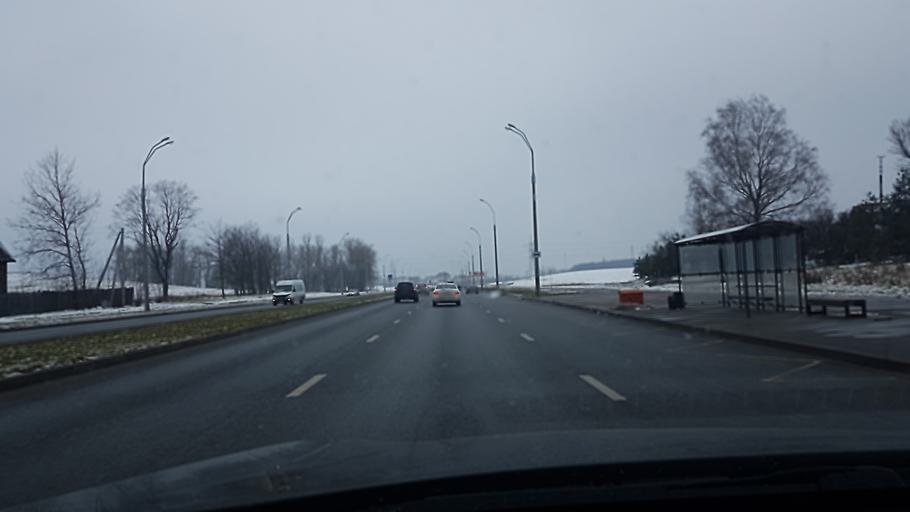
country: BY
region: Minsk
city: Minsk
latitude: 53.9442
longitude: 27.5399
